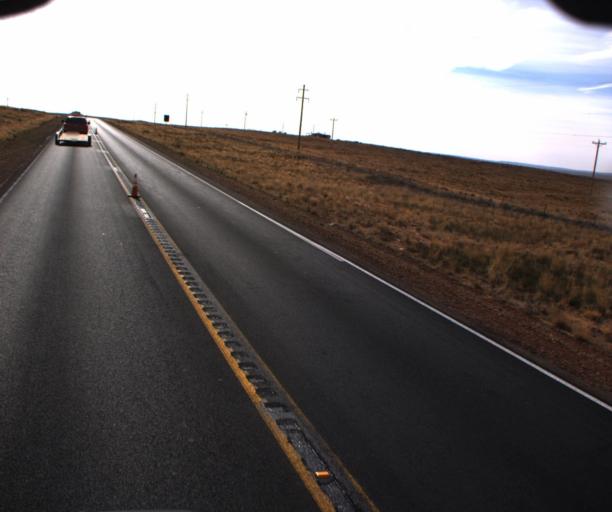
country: US
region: Arizona
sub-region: Apache County
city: Chinle
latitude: 36.0919
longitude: -109.6237
